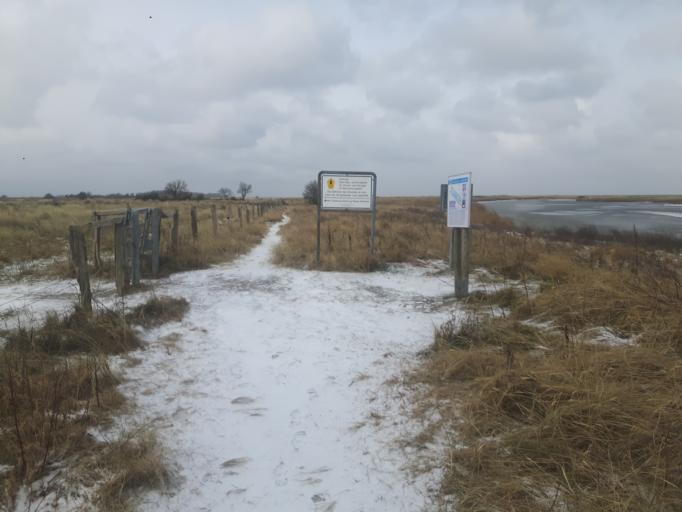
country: DE
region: Schleswig-Holstein
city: Fehmarn
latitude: 54.5110
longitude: 11.1915
